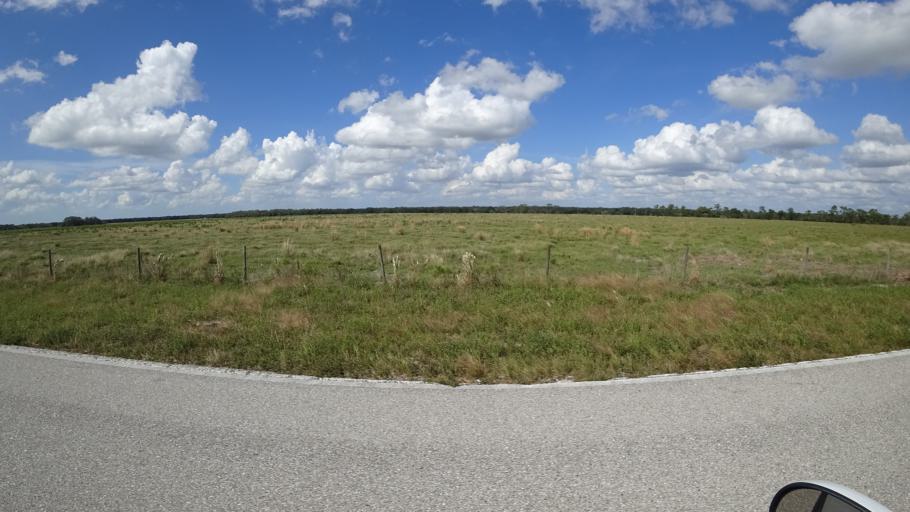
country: US
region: Florida
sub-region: Sarasota County
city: Lake Sarasota
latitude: 27.3163
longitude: -82.1759
